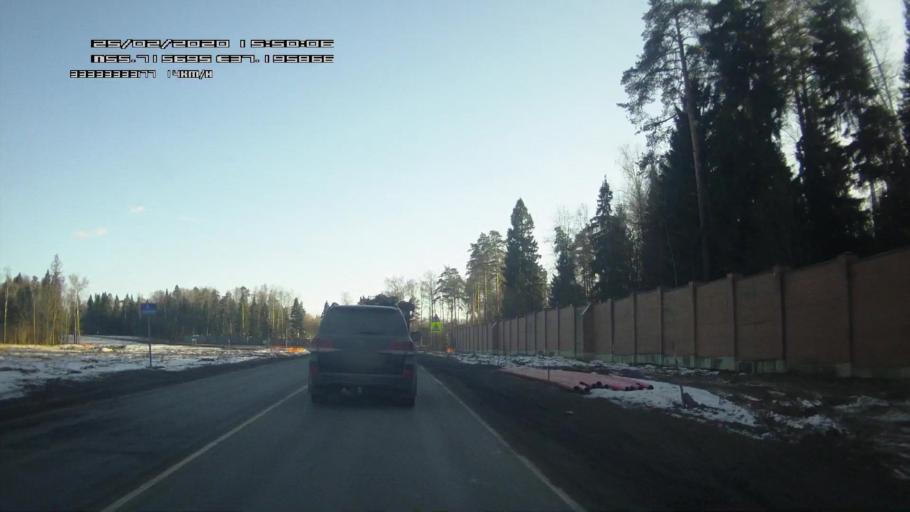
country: RU
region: Moskovskaya
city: Gorki Vtoryye
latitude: 55.7159
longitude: 37.1958
